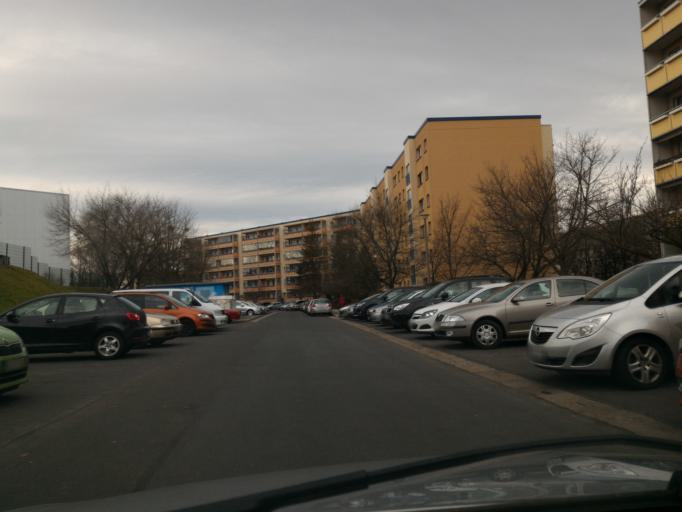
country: DE
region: Saxony
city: Bannewitz
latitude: 51.0201
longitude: 13.7168
